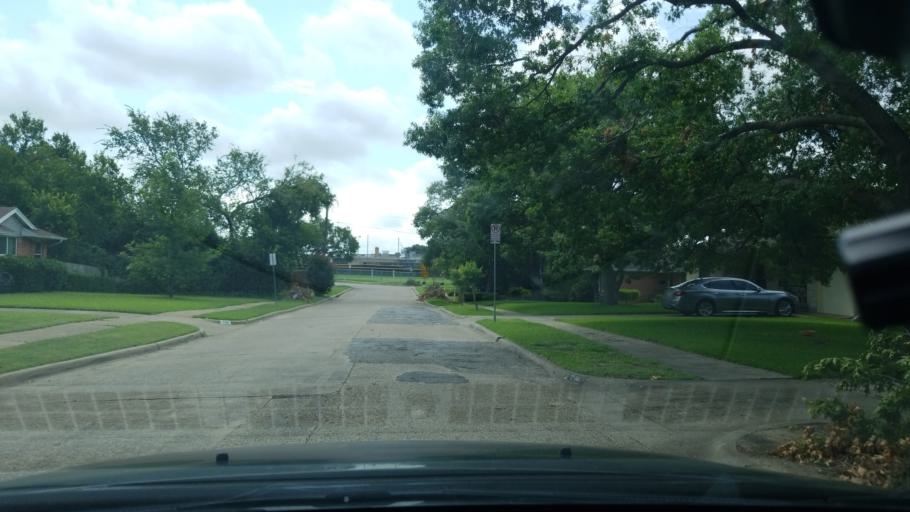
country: US
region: Texas
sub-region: Dallas County
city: Garland
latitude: 32.8296
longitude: -96.6821
